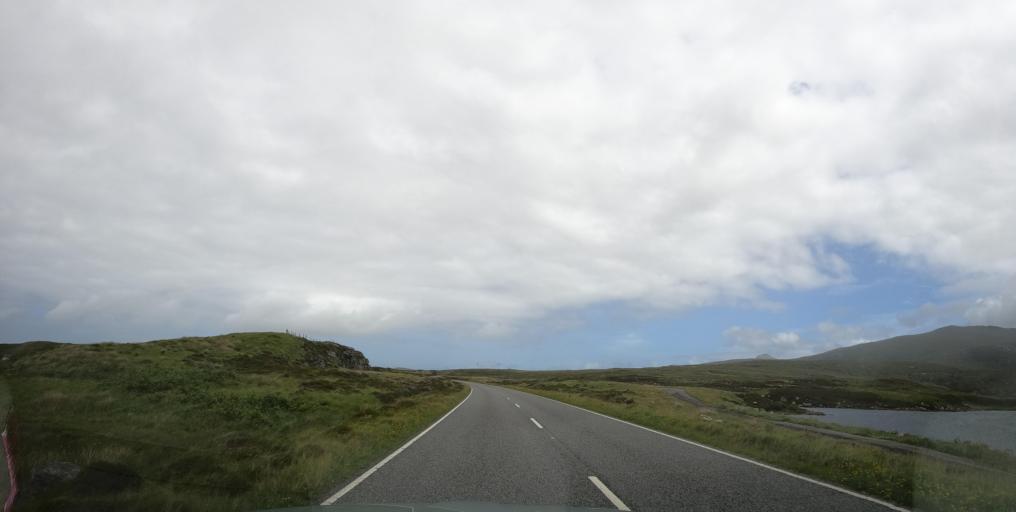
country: GB
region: Scotland
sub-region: Eilean Siar
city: Isle of South Uist
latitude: 57.2578
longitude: -7.3720
